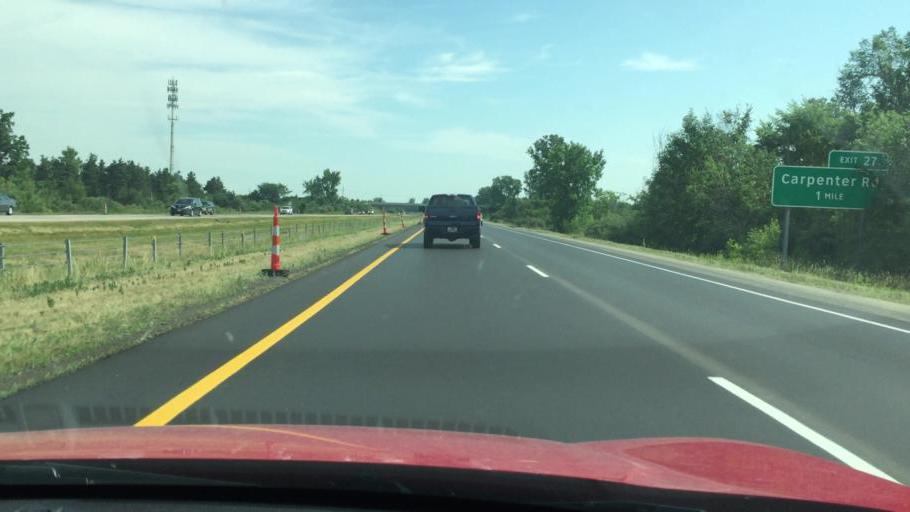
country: US
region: Michigan
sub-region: Washtenaw County
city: Milan
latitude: 42.1182
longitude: -83.6828
